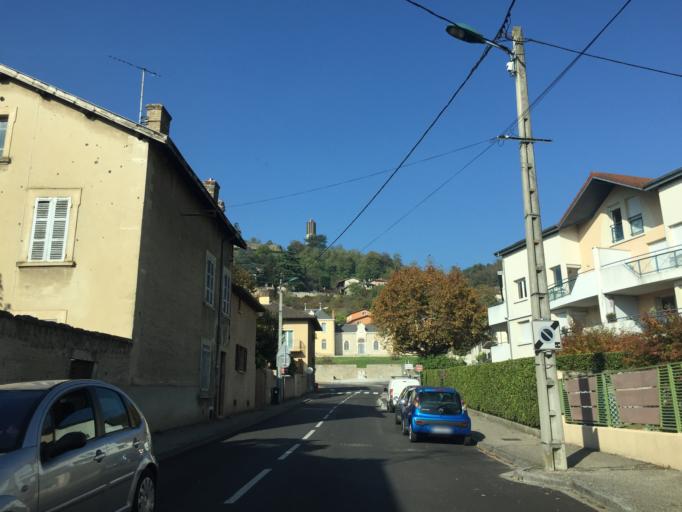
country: FR
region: Rhone-Alpes
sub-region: Departement de l'Ain
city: Miribel
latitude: 45.8262
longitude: 4.9533
